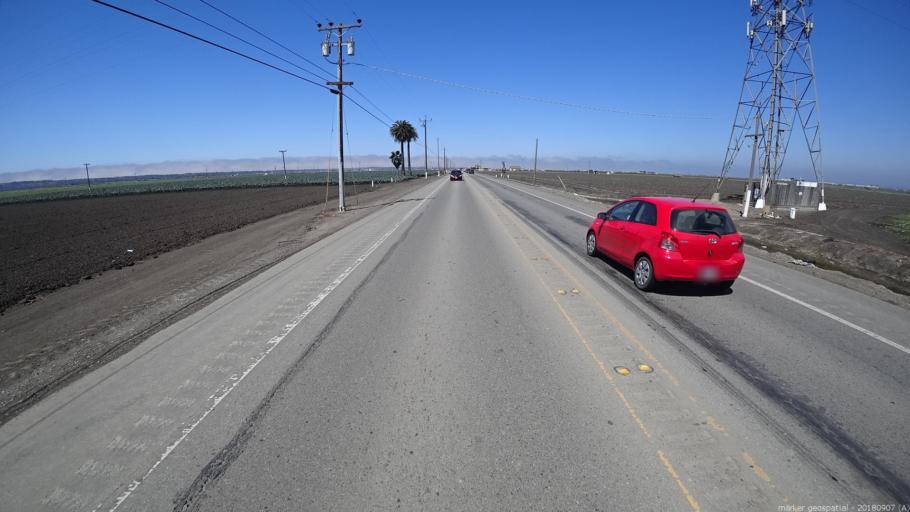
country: US
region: California
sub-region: Monterey County
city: Boronda
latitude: 36.6740
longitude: -121.6979
